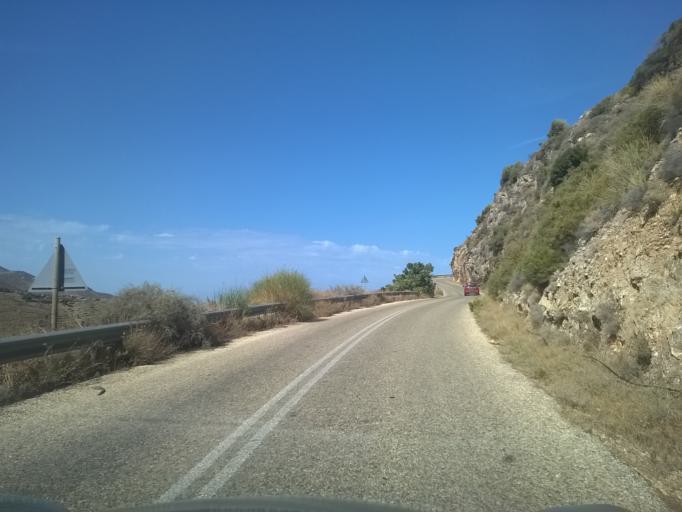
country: GR
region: South Aegean
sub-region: Nomos Kykladon
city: Filotion
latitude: 37.1539
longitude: 25.5495
